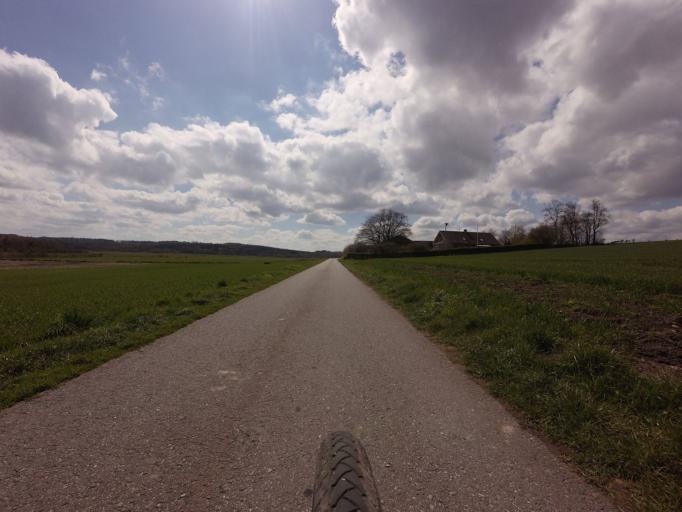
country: DK
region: North Denmark
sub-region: Mariagerfjord Kommune
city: Hadsund
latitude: 56.8539
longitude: 10.0993
